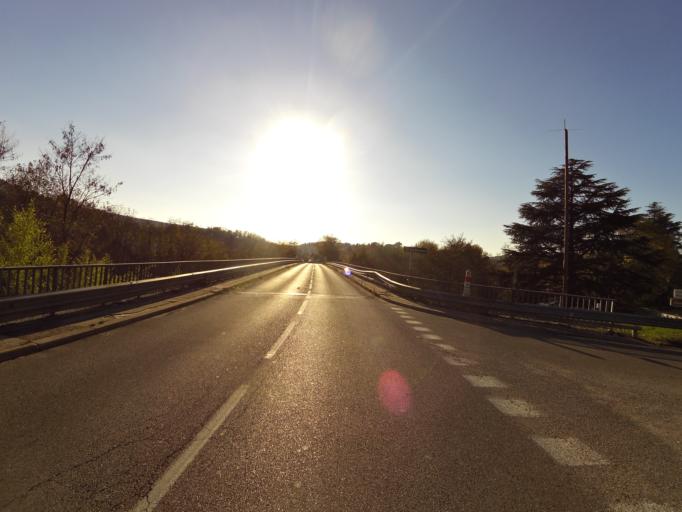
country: FR
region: Rhone-Alpes
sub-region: Departement de l'Ardeche
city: Rosieres
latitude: 44.4817
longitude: 4.2518
